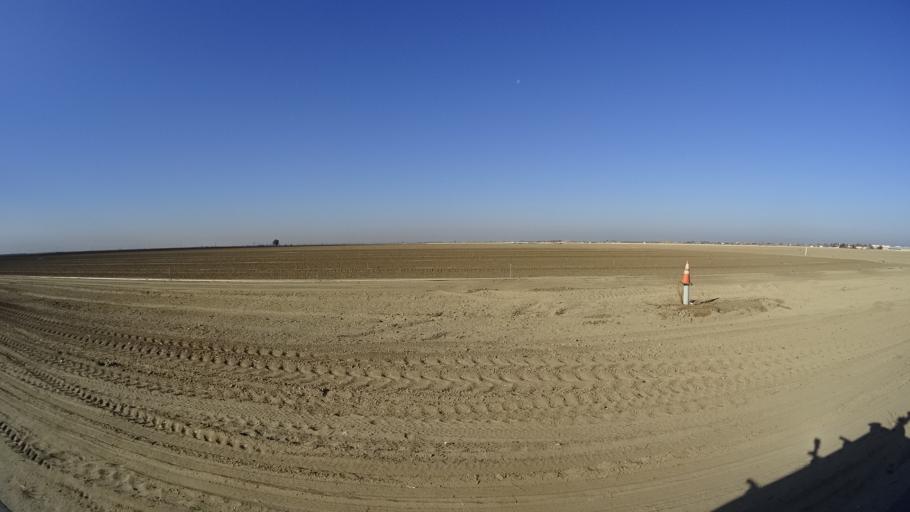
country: US
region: California
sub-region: Kern County
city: Rosedale
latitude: 35.3321
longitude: -119.1457
